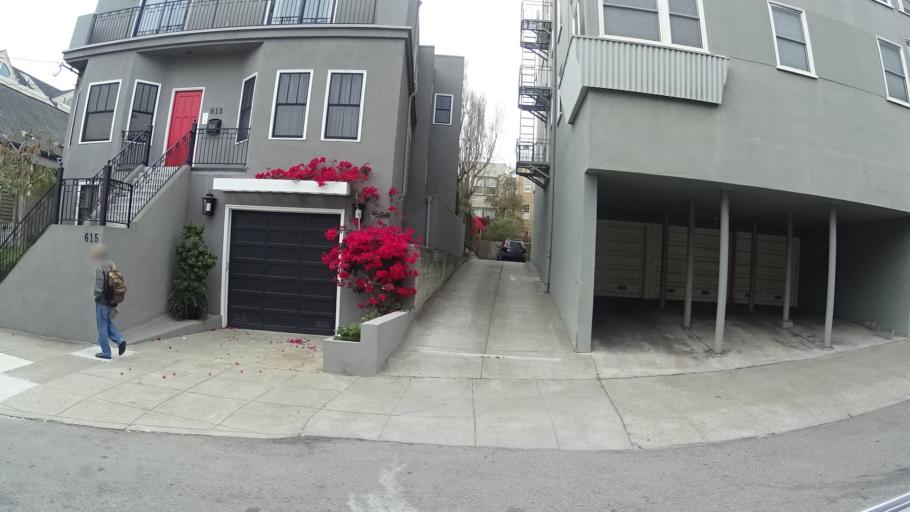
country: US
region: California
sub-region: San Francisco County
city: San Francisco
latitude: 37.7837
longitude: -122.4536
